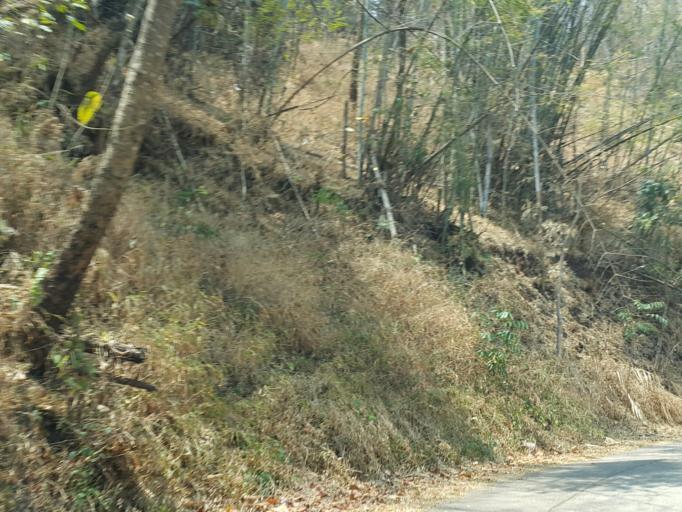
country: TH
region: Chiang Mai
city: Samoeng
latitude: 18.8031
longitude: 98.8070
